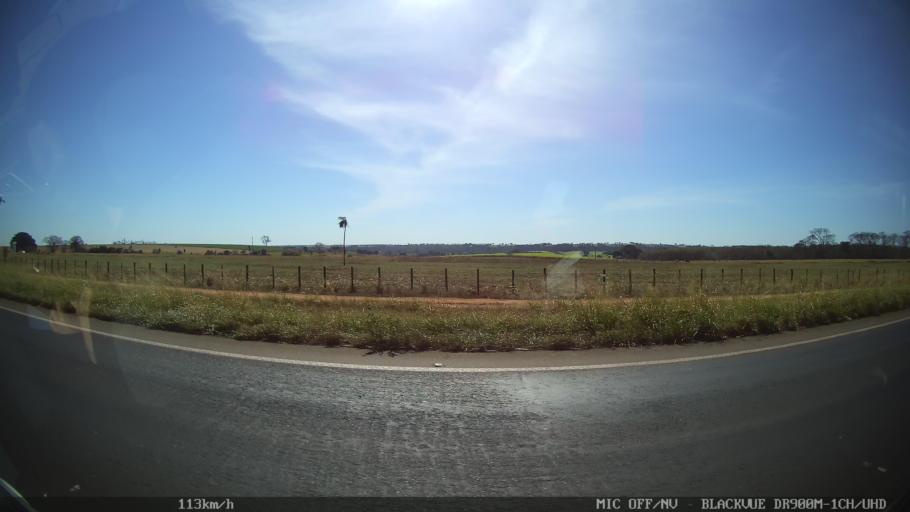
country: BR
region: Sao Paulo
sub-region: Olimpia
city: Olimpia
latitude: -20.6217
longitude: -48.7690
